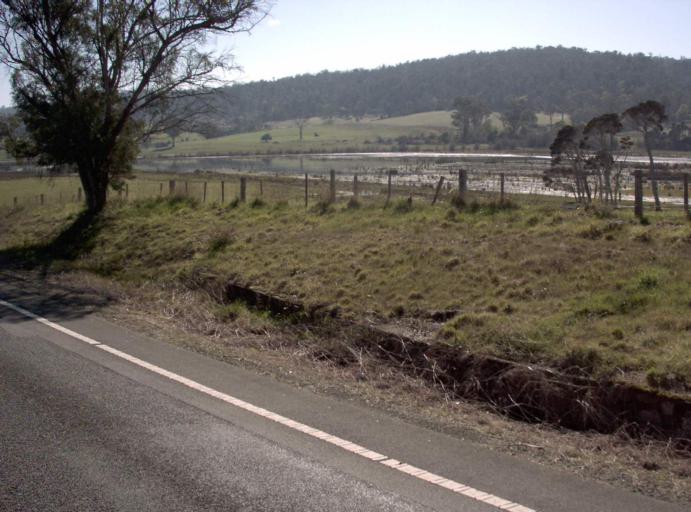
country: AU
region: Tasmania
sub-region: Launceston
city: Mayfield
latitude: -41.3210
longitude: 147.0602
